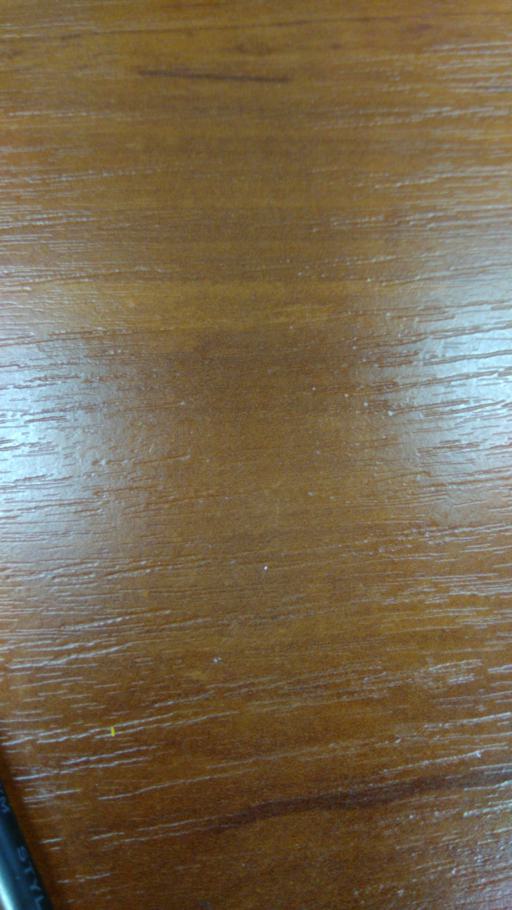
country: RU
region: Tverskaya
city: Emmaus
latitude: 56.7820
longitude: 36.1012
